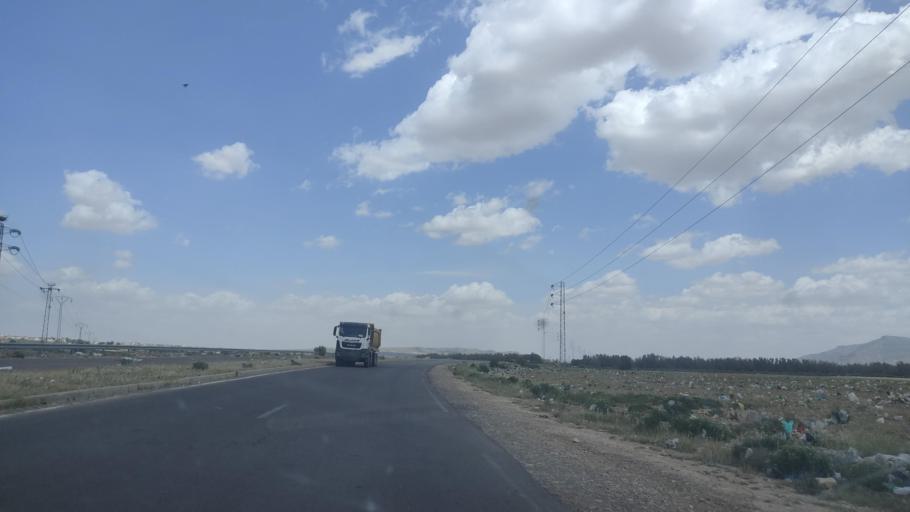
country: TN
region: Al Qasrayn
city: Kasserine
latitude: 35.1995
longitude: 8.8613
